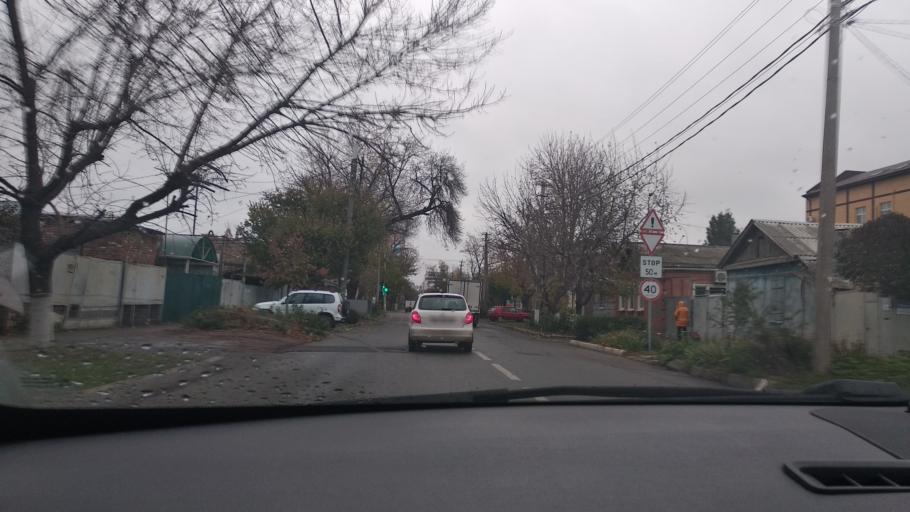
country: RU
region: Krasnodarskiy
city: Krasnodar
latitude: 45.0334
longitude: 38.9847
